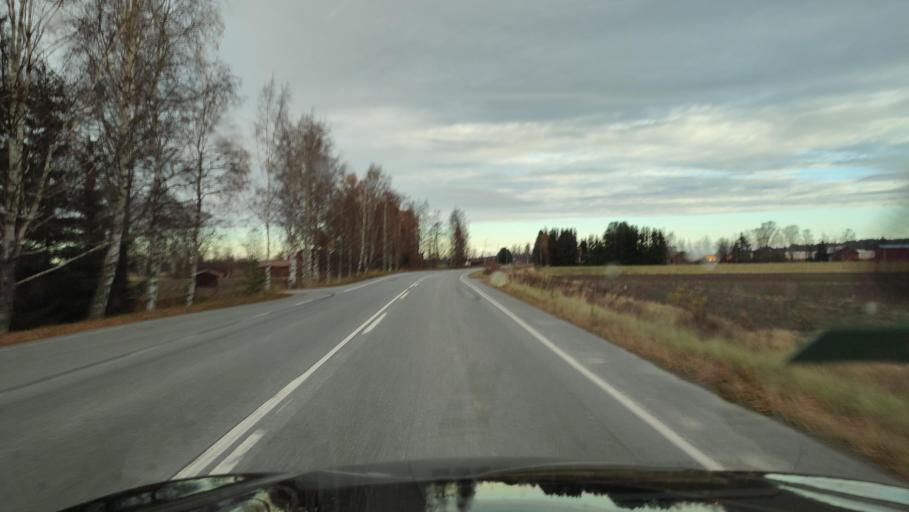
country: FI
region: Ostrobothnia
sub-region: Sydosterbotten
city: Naerpes
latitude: 62.4524
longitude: 21.3531
